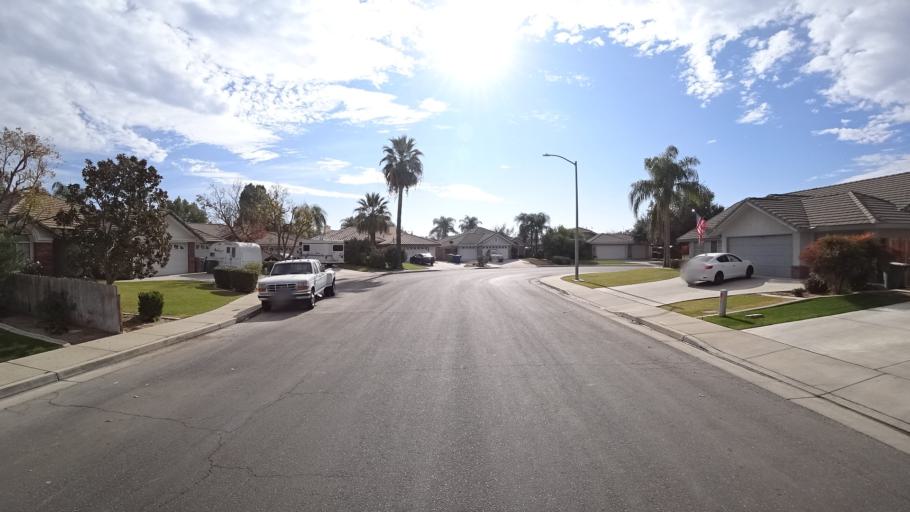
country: US
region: California
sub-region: Kern County
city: Greenacres
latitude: 35.4070
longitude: -119.1239
